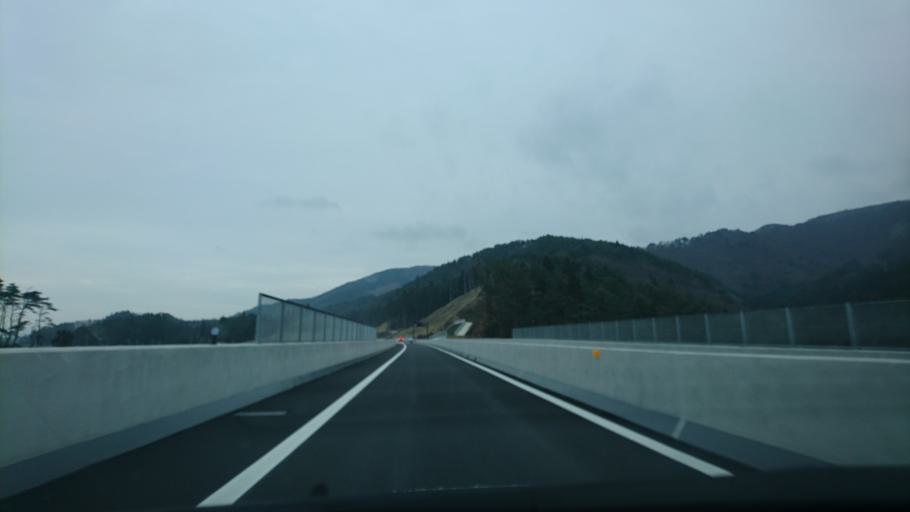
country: JP
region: Iwate
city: Ofunato
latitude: 38.9654
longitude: 141.6244
